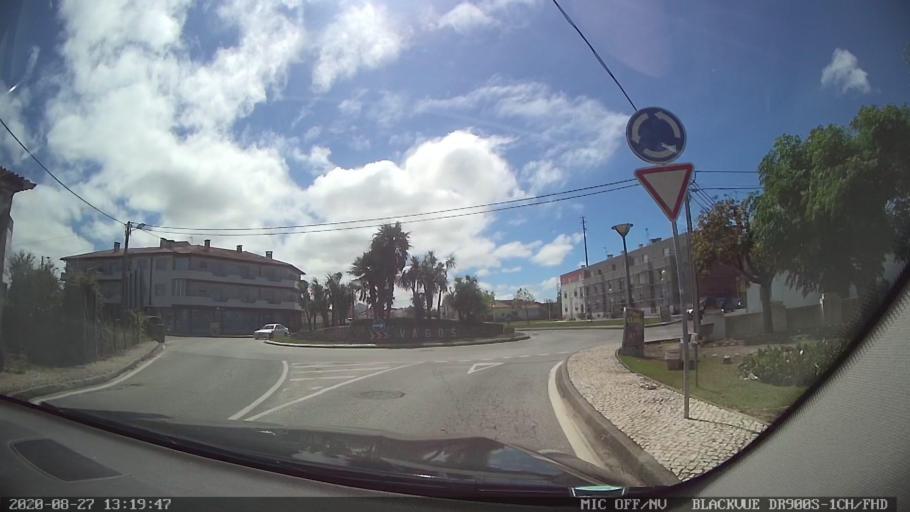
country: PT
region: Aveiro
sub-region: Vagos
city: Vagos
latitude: 40.5609
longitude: -8.6825
